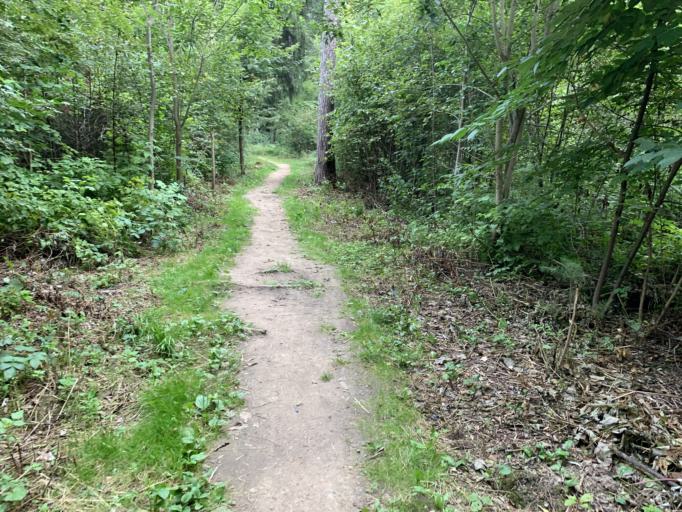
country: RU
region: Moskovskaya
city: Mamontovka
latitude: 55.9922
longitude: 37.8088
